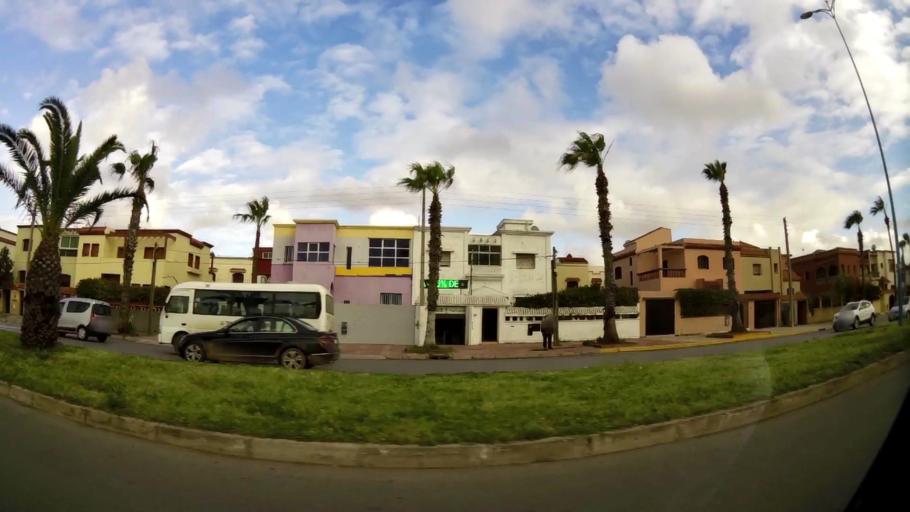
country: MA
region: Grand Casablanca
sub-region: Mohammedia
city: Mohammedia
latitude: 33.6952
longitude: -7.3728
